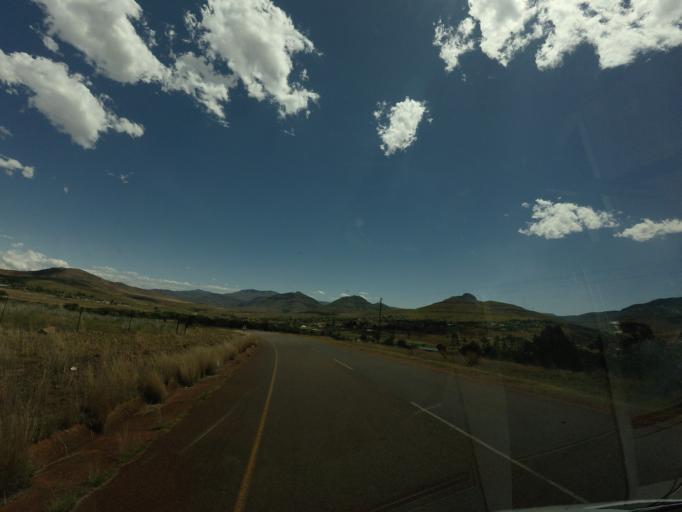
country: ZA
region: Mpumalanga
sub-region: Ehlanzeni District
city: Graksop
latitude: -24.6660
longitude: 30.8103
